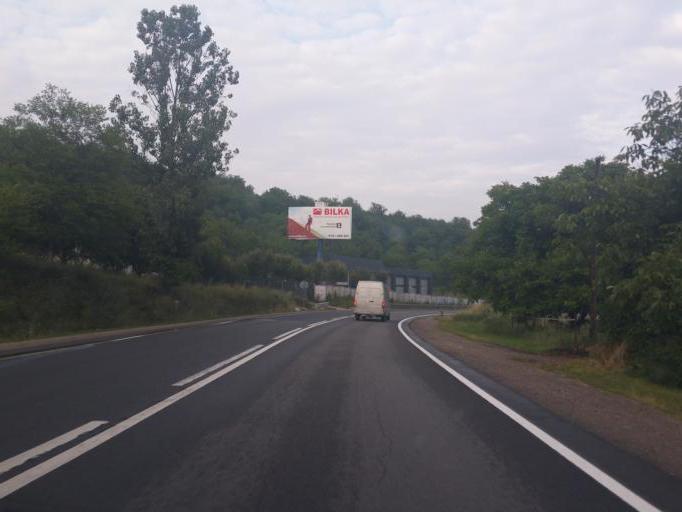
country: RO
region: Cluj
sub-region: Comuna Baciu
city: Baciu
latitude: 46.8001
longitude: 23.5020
